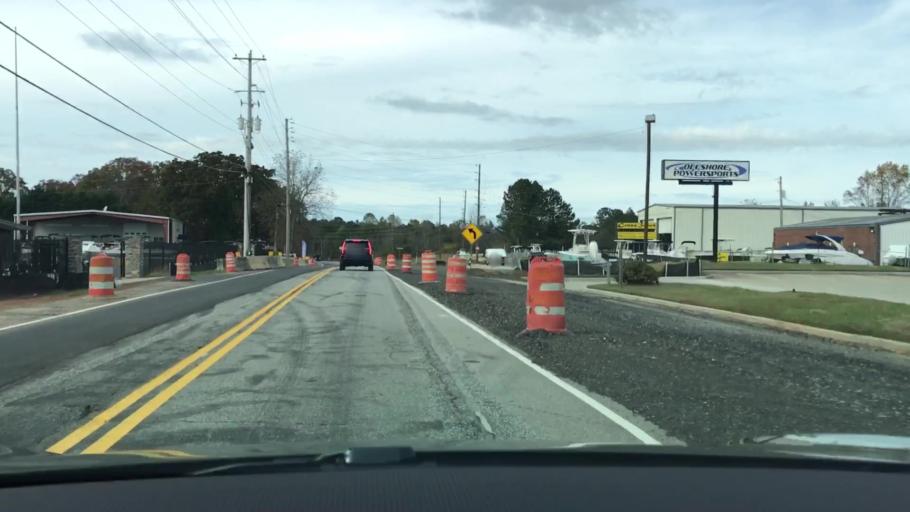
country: US
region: Georgia
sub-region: Gwinnett County
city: Buford
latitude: 34.1558
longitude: -83.9884
